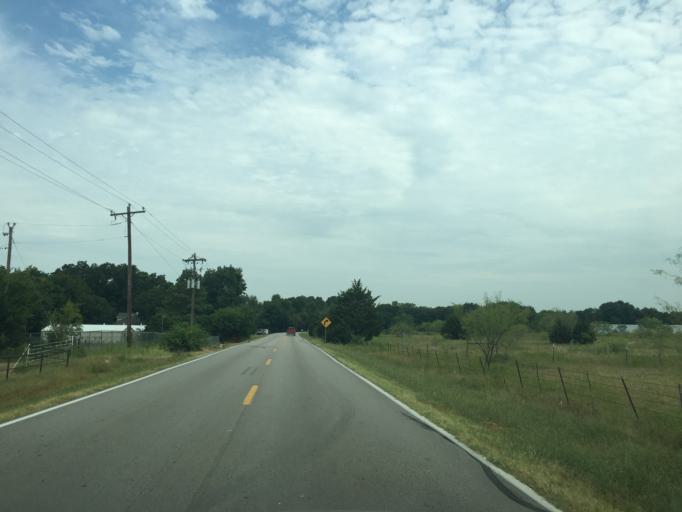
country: US
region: Texas
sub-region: Collin County
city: Wylie
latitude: 32.9734
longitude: -96.5255
